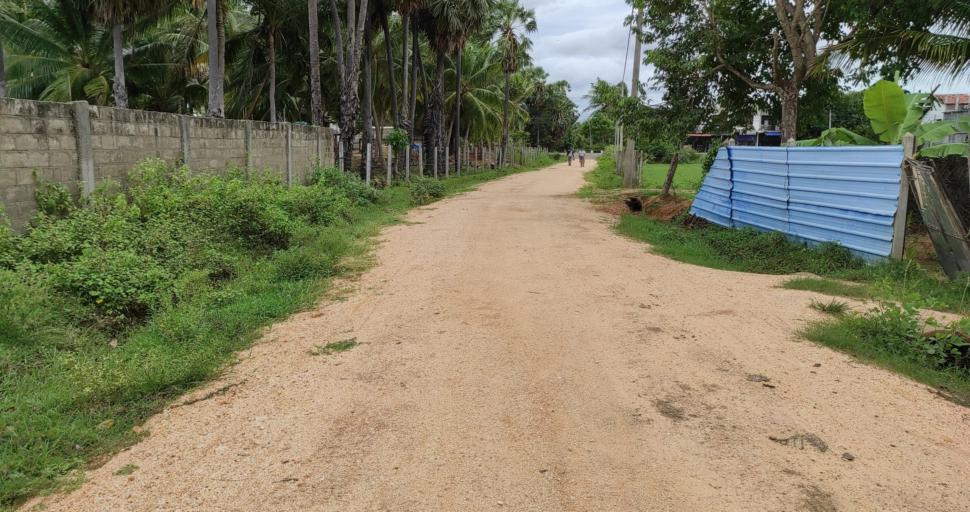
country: LK
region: Eastern Province
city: Trincomalee
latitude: 8.4445
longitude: 81.0536
